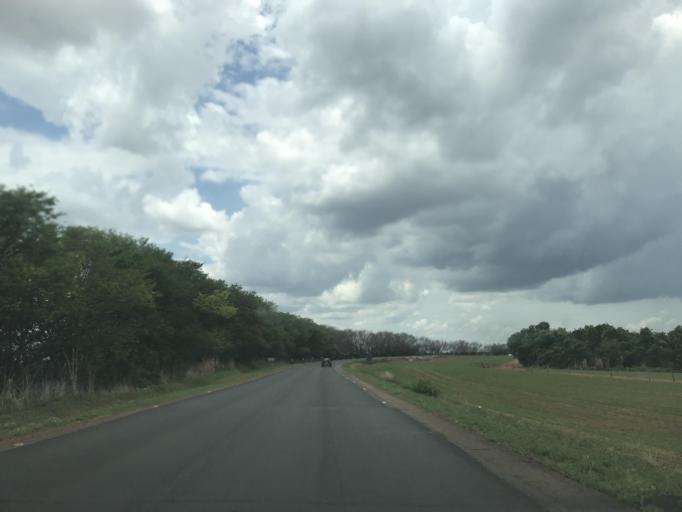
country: BR
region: Goias
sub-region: Vianopolis
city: Vianopolis
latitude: -16.8050
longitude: -48.5188
